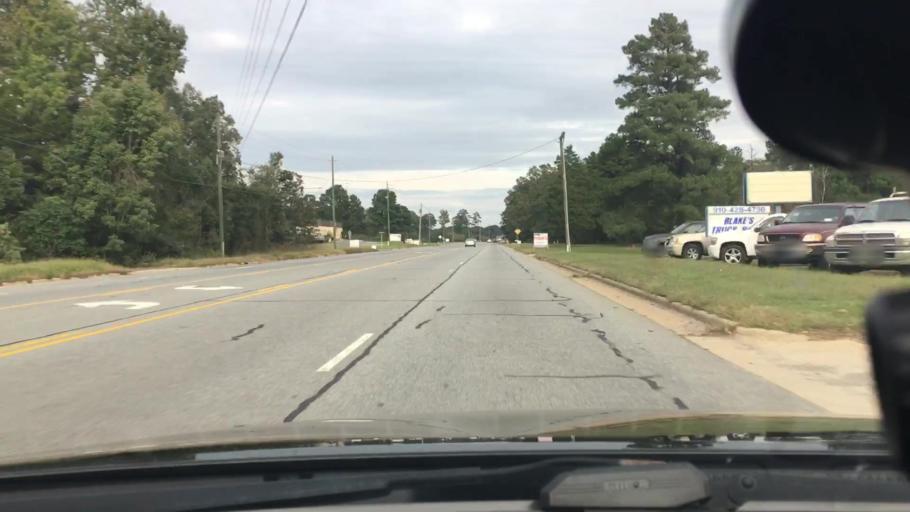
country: US
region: North Carolina
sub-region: Montgomery County
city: Biscoe
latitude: 35.3574
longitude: -79.8046
